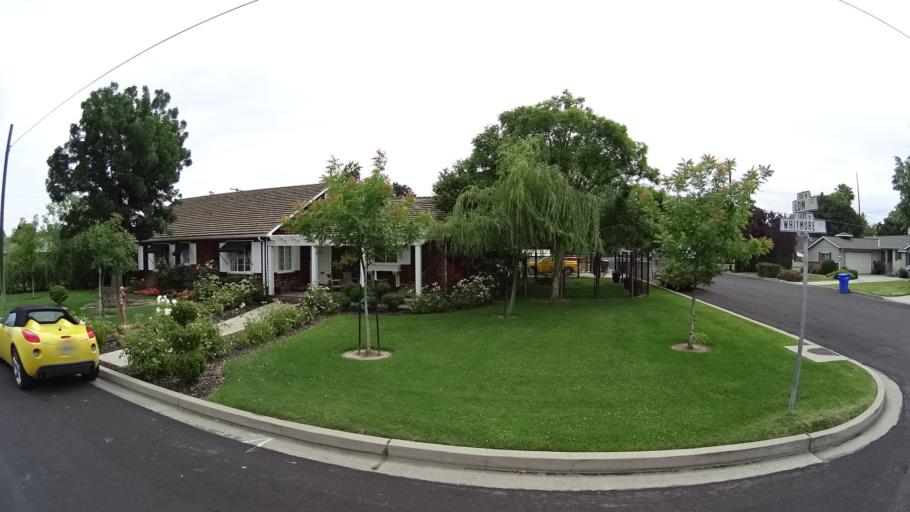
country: US
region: California
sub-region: Kings County
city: Hanford
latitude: 36.3419
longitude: -119.6537
